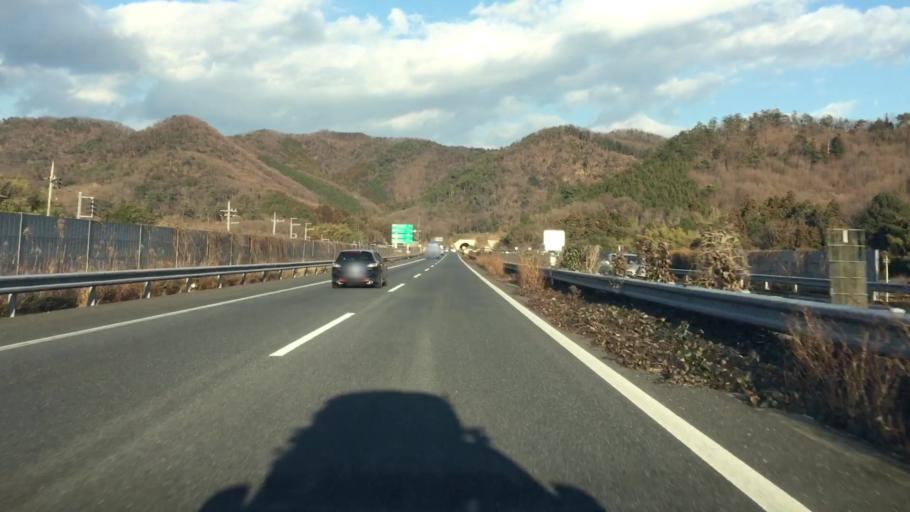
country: JP
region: Tochigi
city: Ashikaga
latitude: 36.3653
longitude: 139.4946
